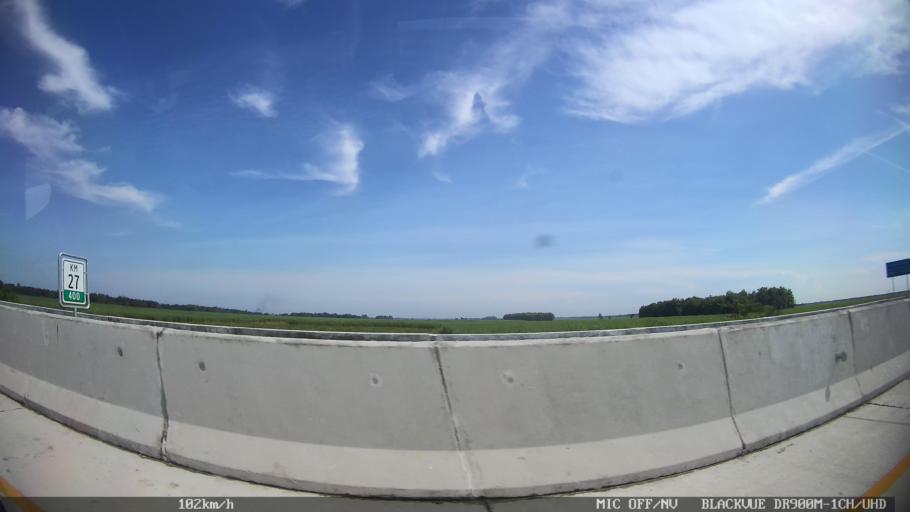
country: ID
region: North Sumatra
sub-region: Kabupaten Langkat
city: Stabat
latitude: 3.7134
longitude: 98.5160
